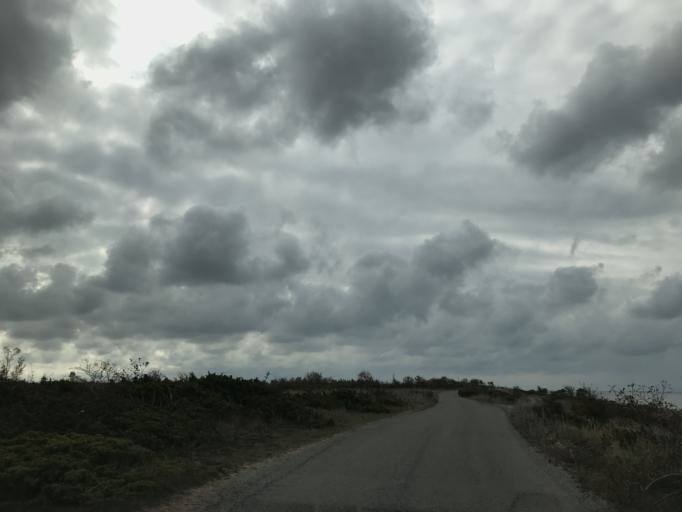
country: SE
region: Kalmar
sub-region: Borgholms Kommun
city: Borgholm
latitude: 57.0456
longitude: 16.8307
